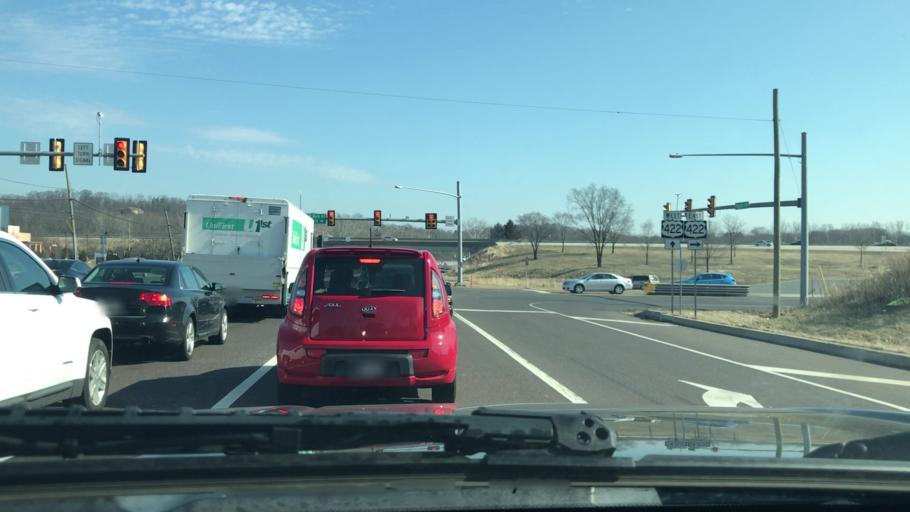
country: US
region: Pennsylvania
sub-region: Montgomery County
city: Audubon
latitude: 40.1338
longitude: -75.4500
